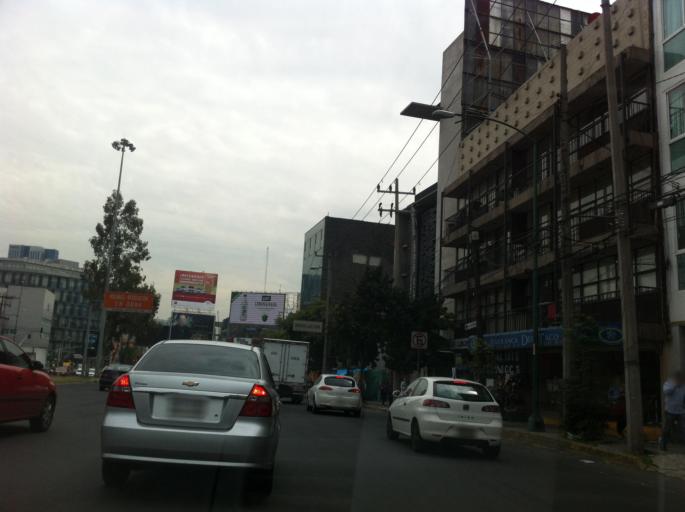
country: MX
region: Mexico City
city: Alvaro Obregon
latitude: 19.3633
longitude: -99.1904
